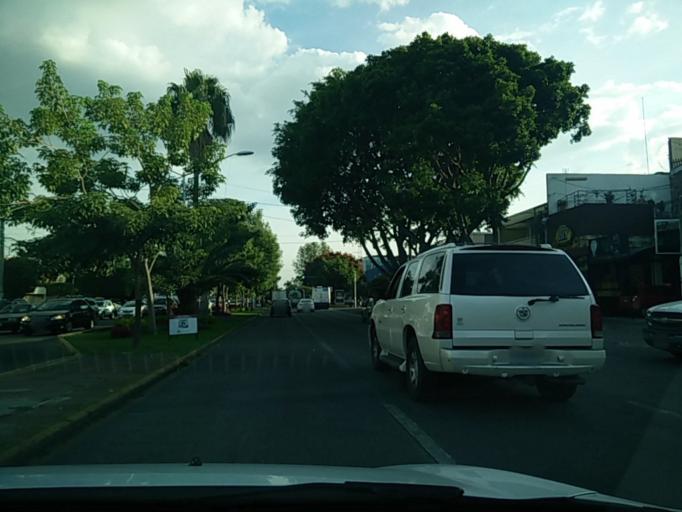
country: MX
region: Jalisco
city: Guadalajara
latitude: 20.6842
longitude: -103.3736
